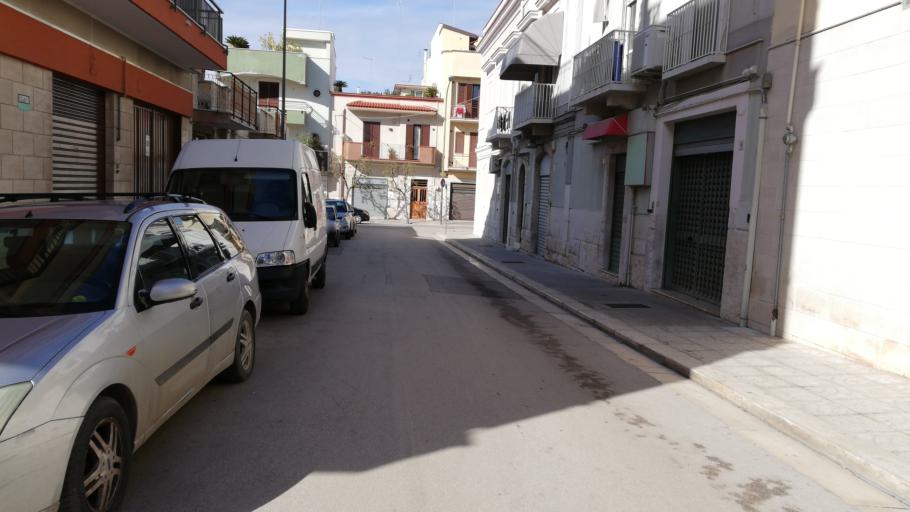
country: IT
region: Apulia
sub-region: Provincia di Barletta - Andria - Trani
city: Andria
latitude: 41.2207
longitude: 16.3028
